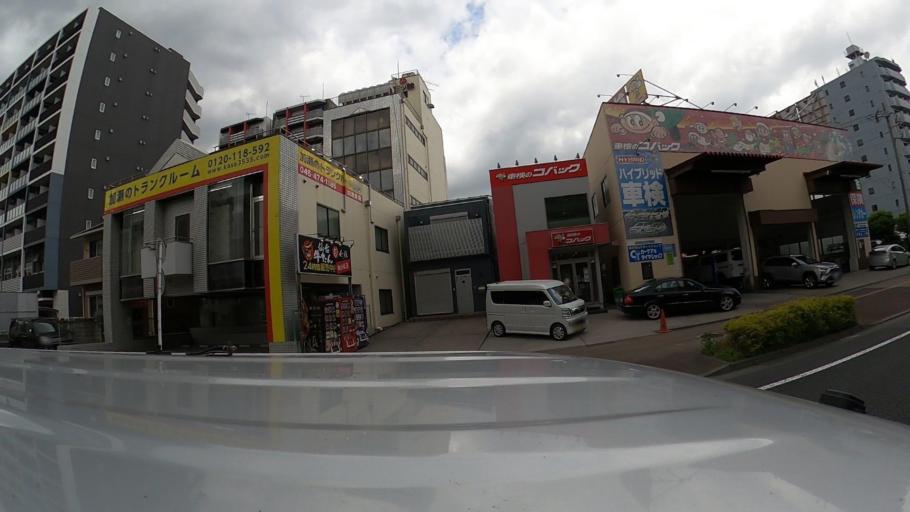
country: JP
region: Kanagawa
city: Yokohama
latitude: 35.4870
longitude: 139.6569
